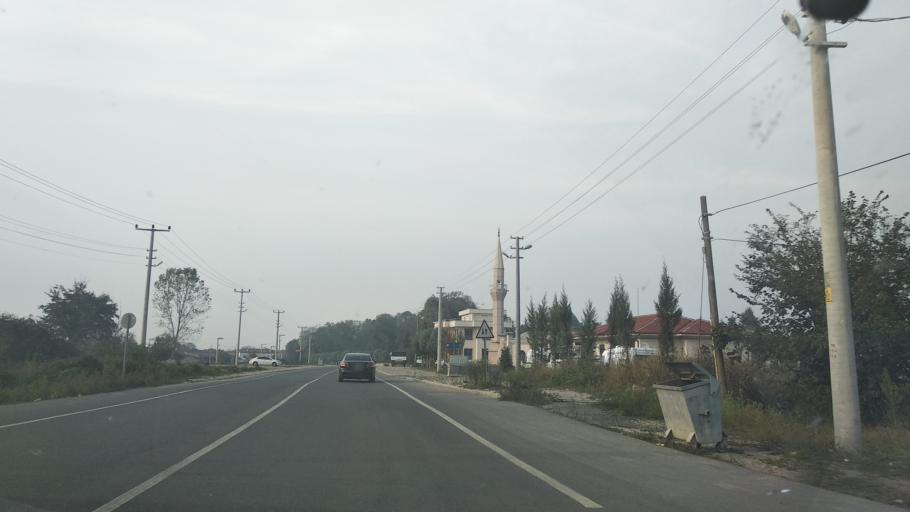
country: TR
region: Duzce
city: Duzce
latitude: 40.8244
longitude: 31.1753
